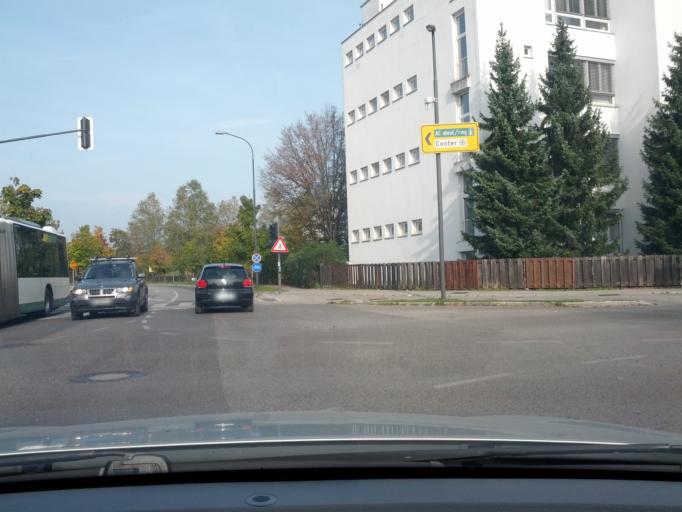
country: SI
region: Ljubljana
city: Ljubljana
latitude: 46.0706
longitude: 14.5188
